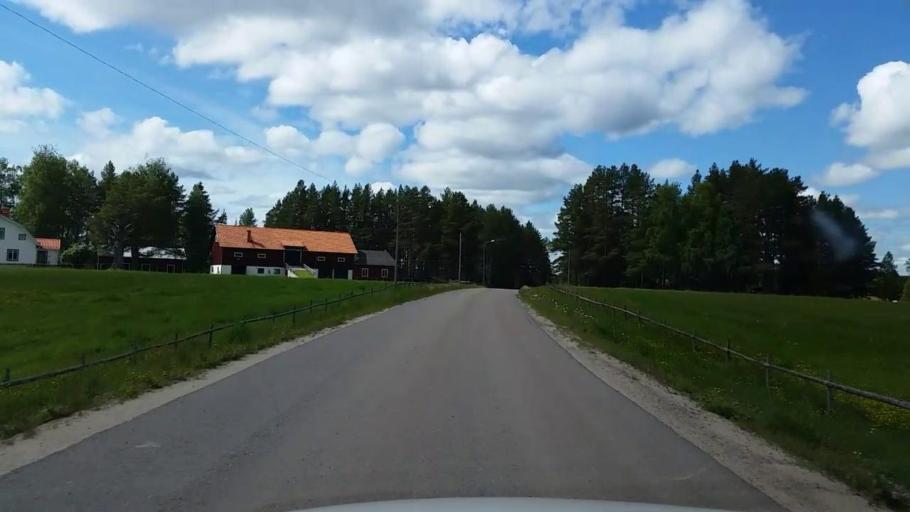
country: SE
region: Gaevleborg
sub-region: Ovanakers Kommun
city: Alfta
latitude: 61.4785
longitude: 15.9984
